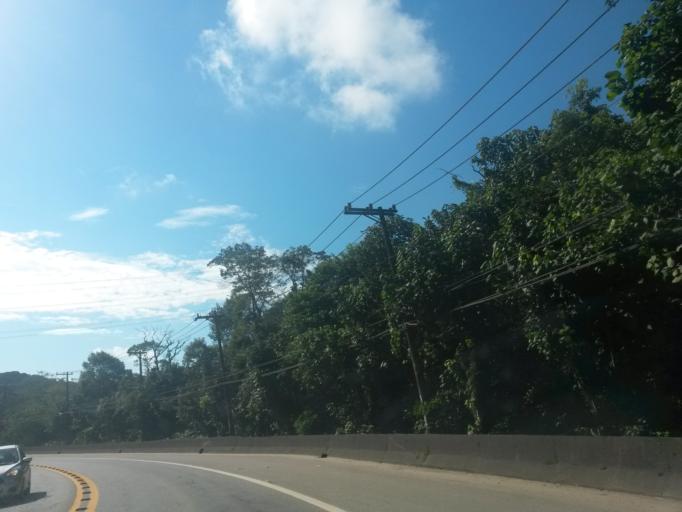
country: BR
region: Sao Paulo
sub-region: Sao Bernardo Do Campo
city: Sao Bernardo do Campo
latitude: -23.7807
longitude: -46.5063
